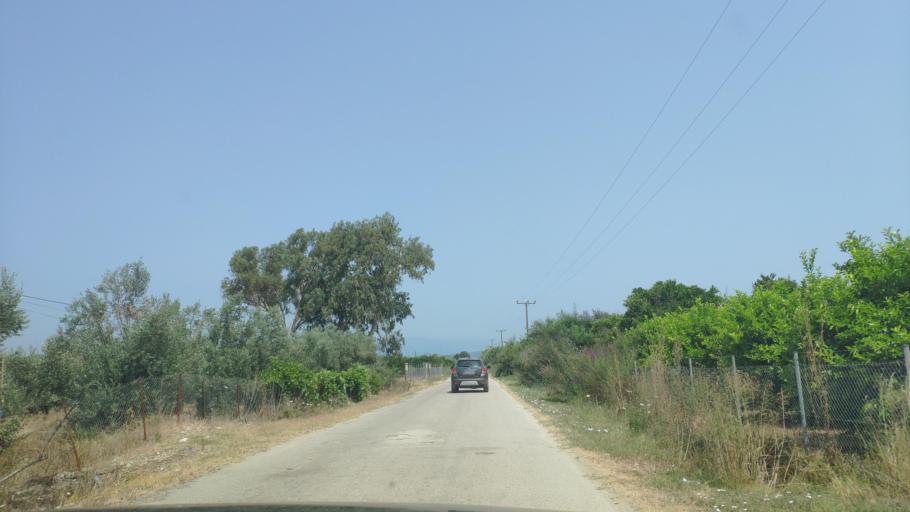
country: GR
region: West Greece
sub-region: Nomos Aitolias kai Akarnanias
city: Menidi
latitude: 39.0542
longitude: 21.0695
